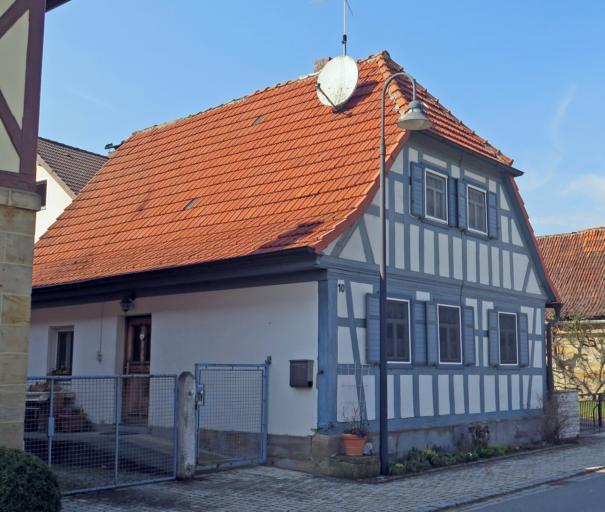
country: DE
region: Bavaria
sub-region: Regierungsbezirk Unterfranken
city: Untermerzbach
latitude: 50.1005
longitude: 10.8564
